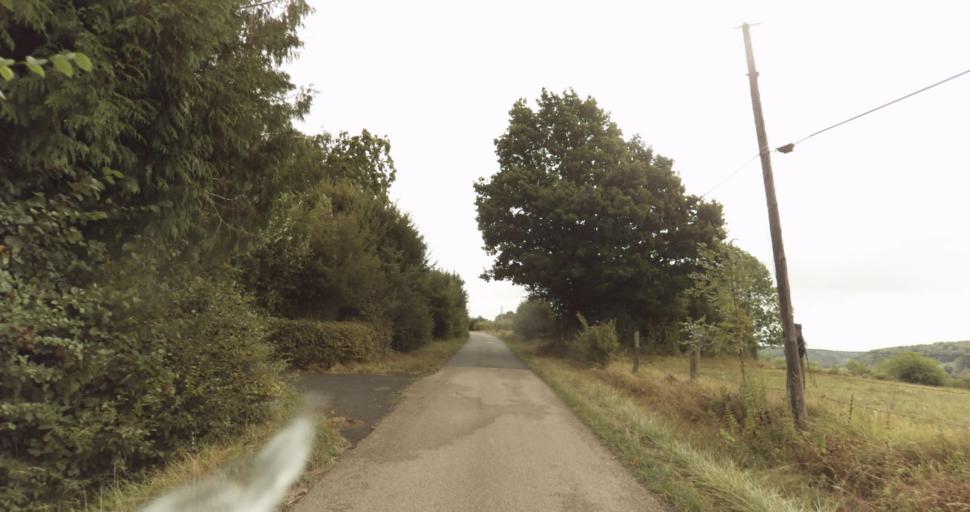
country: FR
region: Lower Normandy
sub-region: Departement de l'Orne
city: Gace
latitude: 48.8716
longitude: 0.2870
